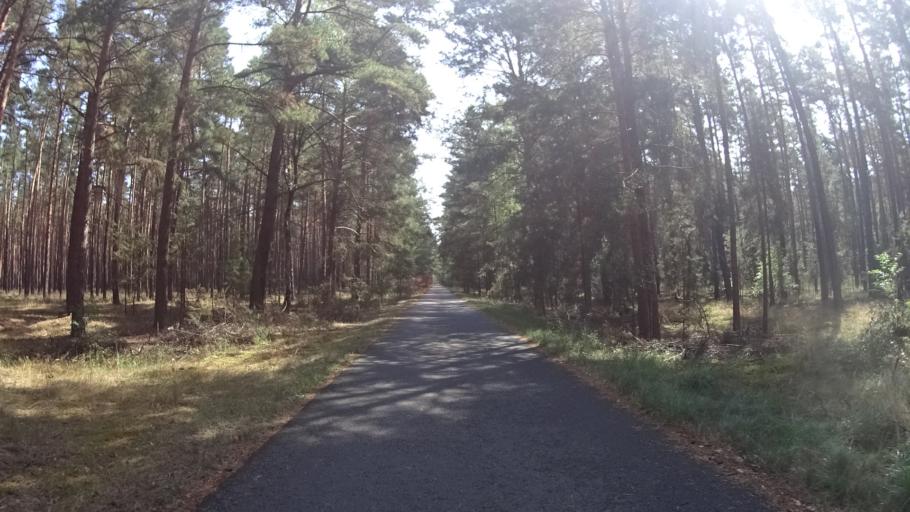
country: DE
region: Brandenburg
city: Briesen
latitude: 51.8085
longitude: 14.2573
